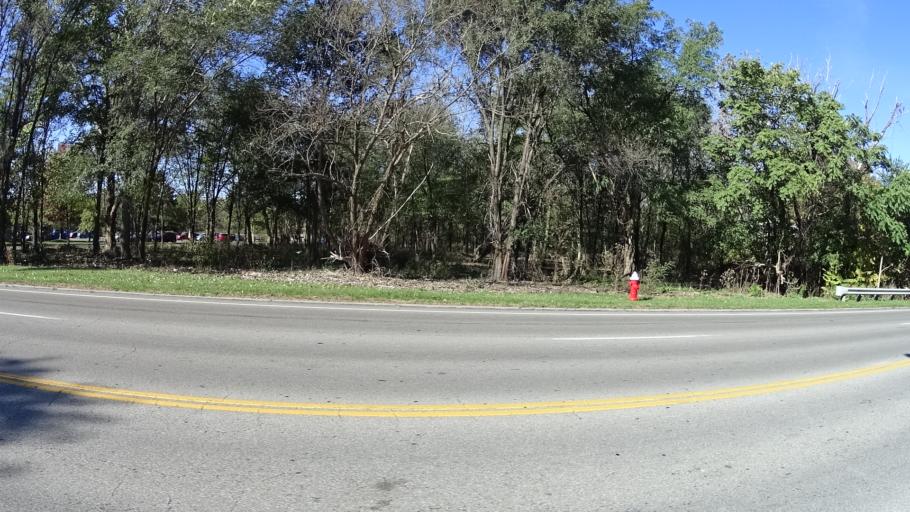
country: US
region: Ohio
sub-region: Lorain County
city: Lorain
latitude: 41.4160
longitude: -82.1629
